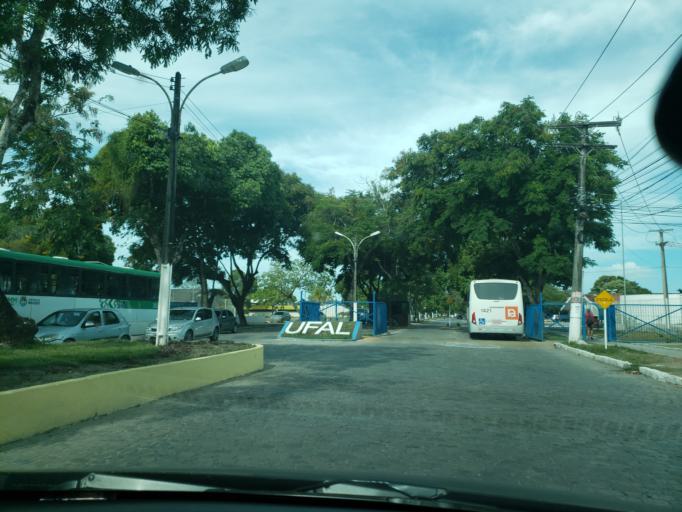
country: BR
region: Alagoas
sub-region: Satuba
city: Satuba
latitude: -9.5573
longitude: -35.7811
